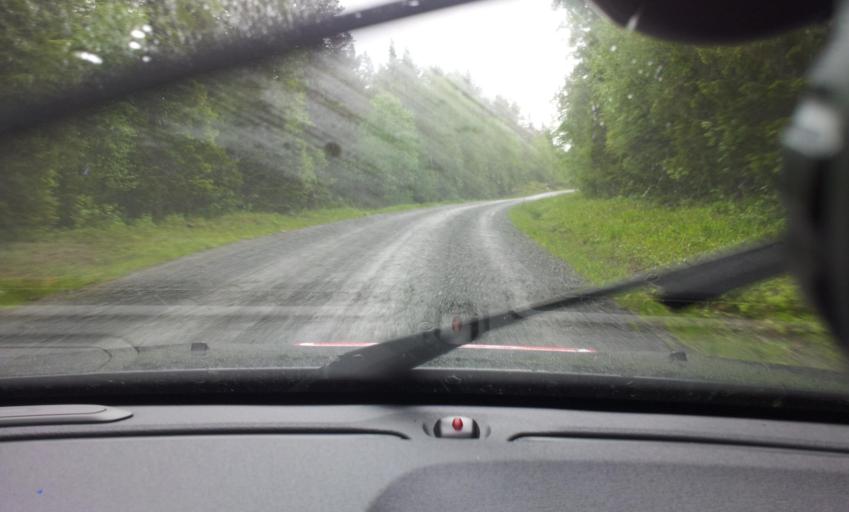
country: SE
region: Jaemtland
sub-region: OEstersunds Kommun
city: Brunflo
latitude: 63.1109
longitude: 15.0915
